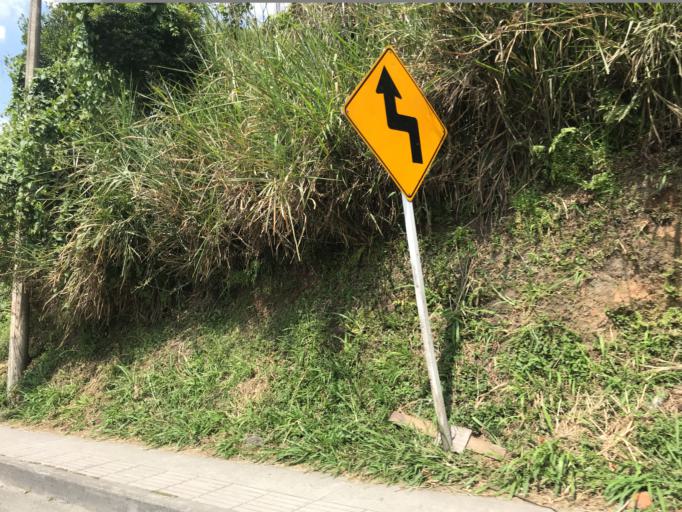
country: CO
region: Quindio
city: Calarca
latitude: 4.5235
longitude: -75.6404
